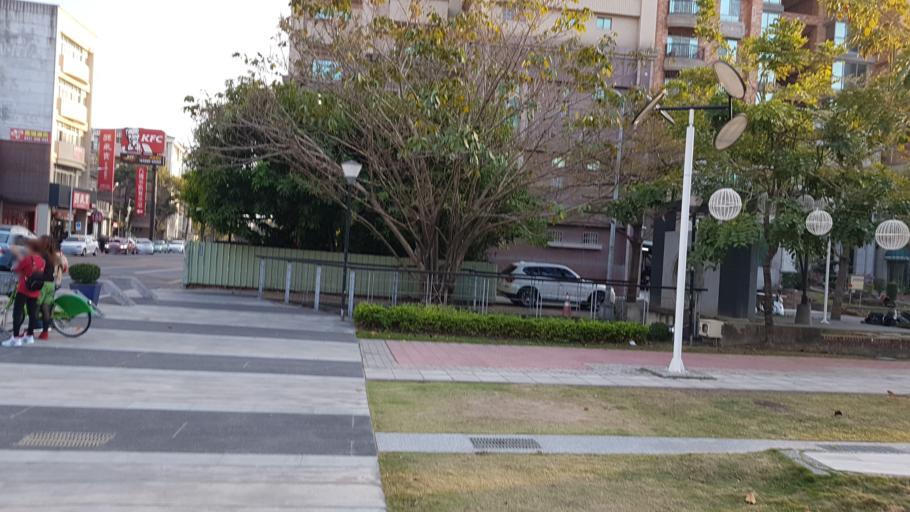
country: TW
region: Taiwan
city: Xinying
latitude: 23.3082
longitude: 120.3160
